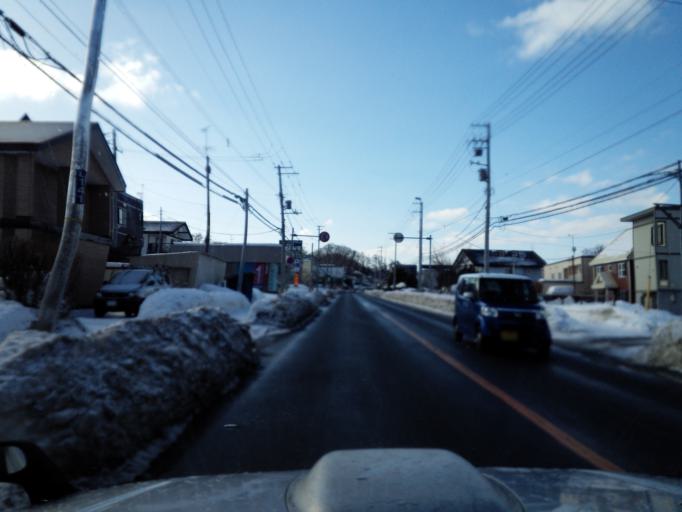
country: JP
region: Hokkaido
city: Sapporo
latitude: 42.9482
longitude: 141.3469
